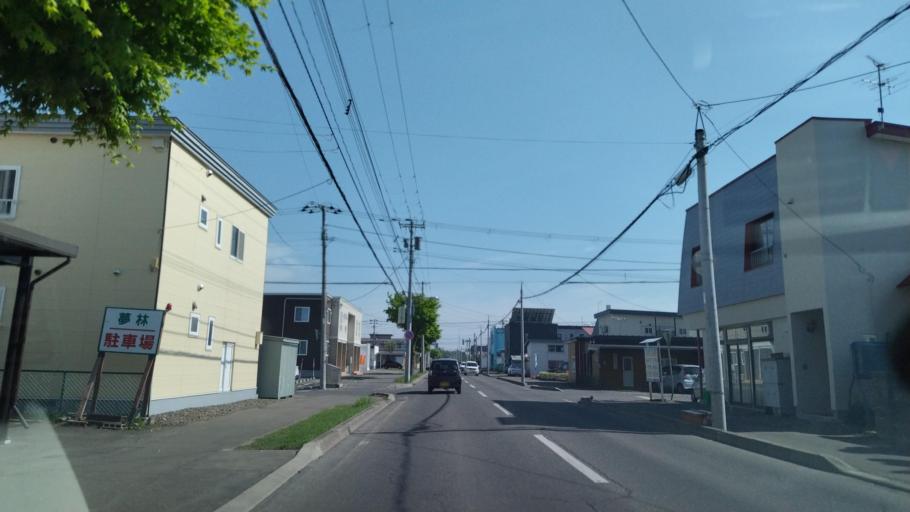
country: JP
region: Hokkaido
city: Obihiro
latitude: 42.8972
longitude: 143.1881
